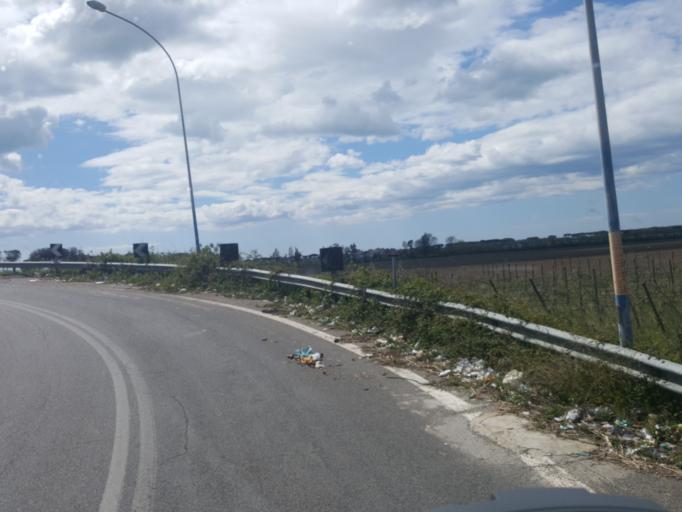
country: IT
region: Campania
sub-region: Provincia di Napoli
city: Masseria Vecchia Ovest
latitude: 40.9343
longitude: 14.0796
